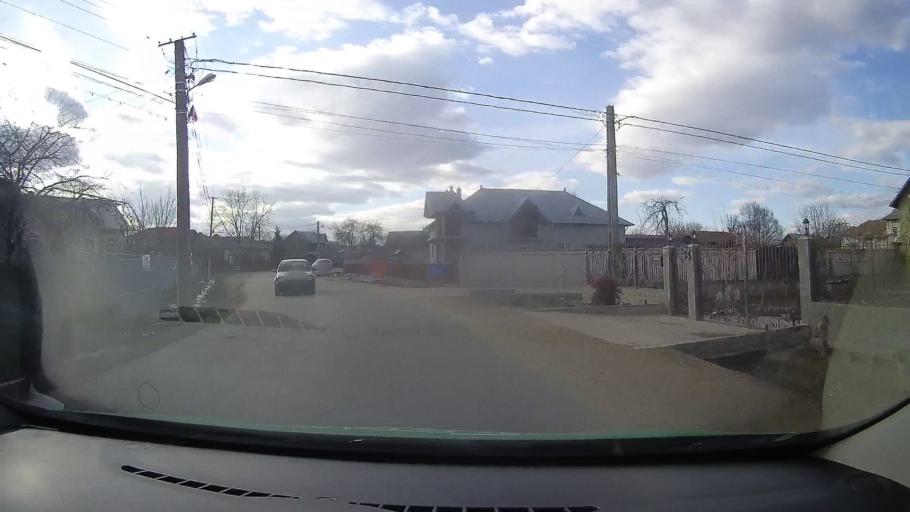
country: RO
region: Dambovita
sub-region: Comuna Ulmi
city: Ulmi
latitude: 44.8808
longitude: 25.5150
